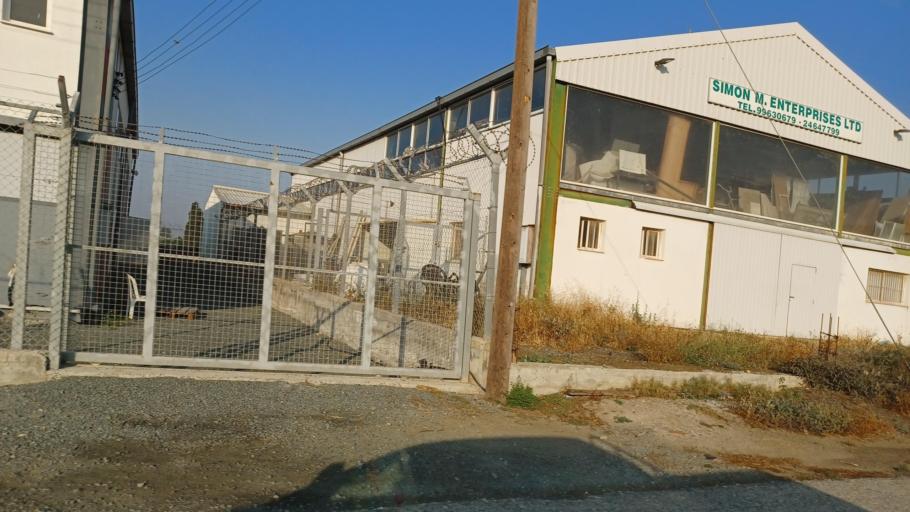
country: CY
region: Larnaka
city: Pyla
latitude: 35.0102
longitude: 33.7010
